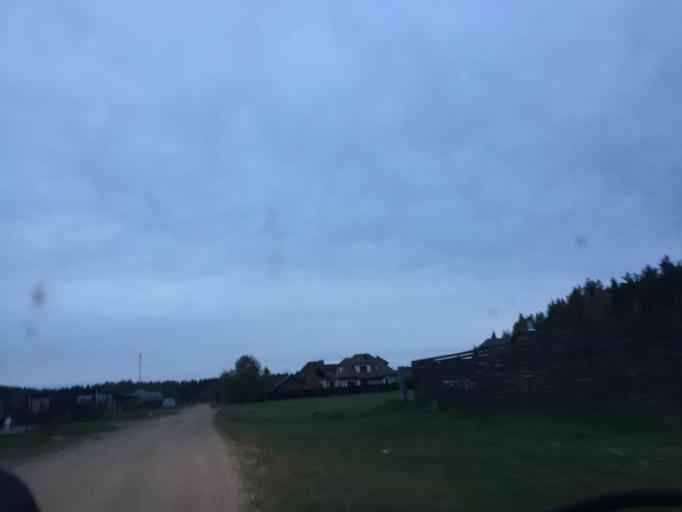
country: LV
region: Adazi
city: Adazi
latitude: 57.0851
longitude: 24.3774
